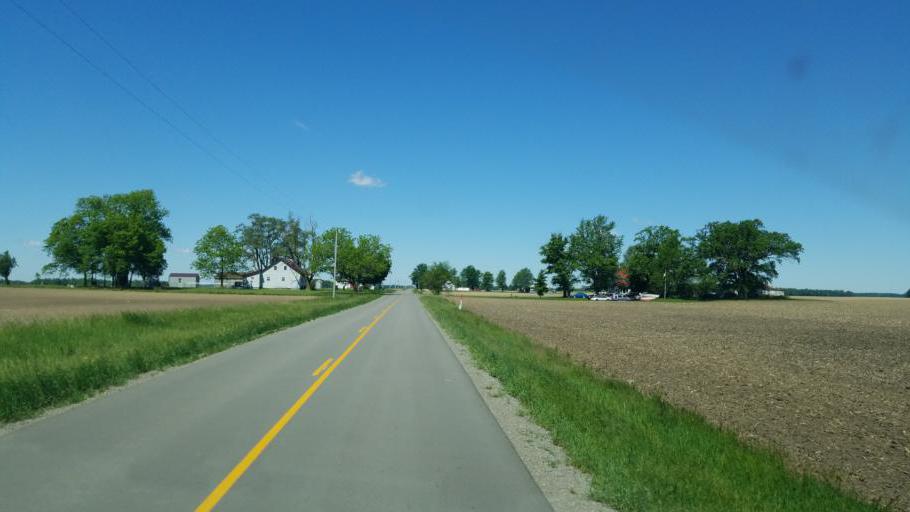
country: US
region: Ohio
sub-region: Logan County
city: Lakeview
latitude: 40.4174
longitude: -83.9516
